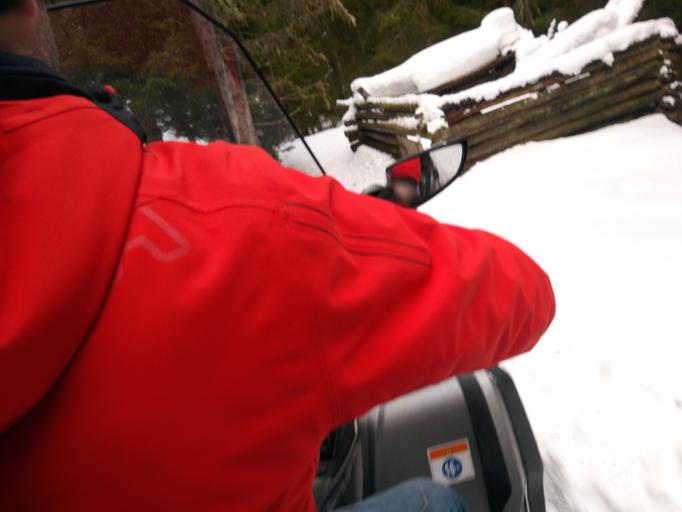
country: IT
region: Veneto
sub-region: Provincia di Belluno
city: Rocca Pietore
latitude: 46.4158
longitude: 11.9848
